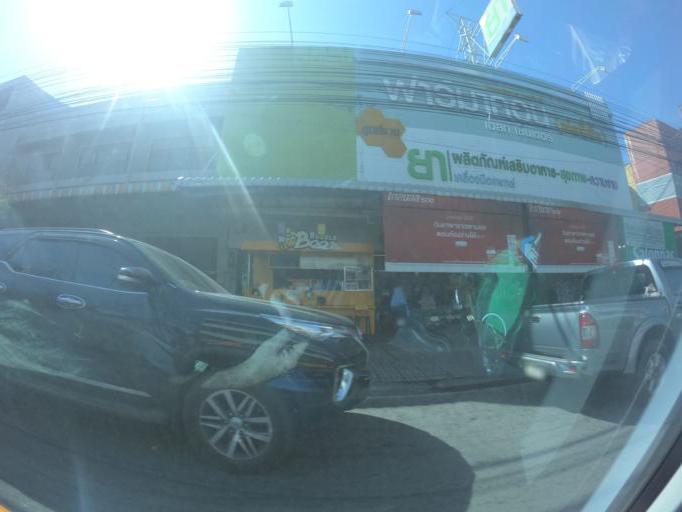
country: TH
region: Khon Kaen
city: Khon Kaen
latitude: 16.3779
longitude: 102.9258
